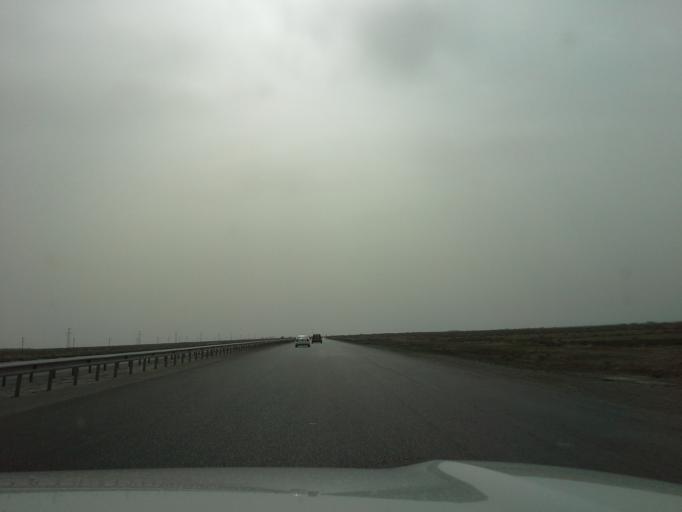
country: IR
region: Razavi Khorasan
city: Dargaz
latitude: 37.5820
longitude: 59.3079
